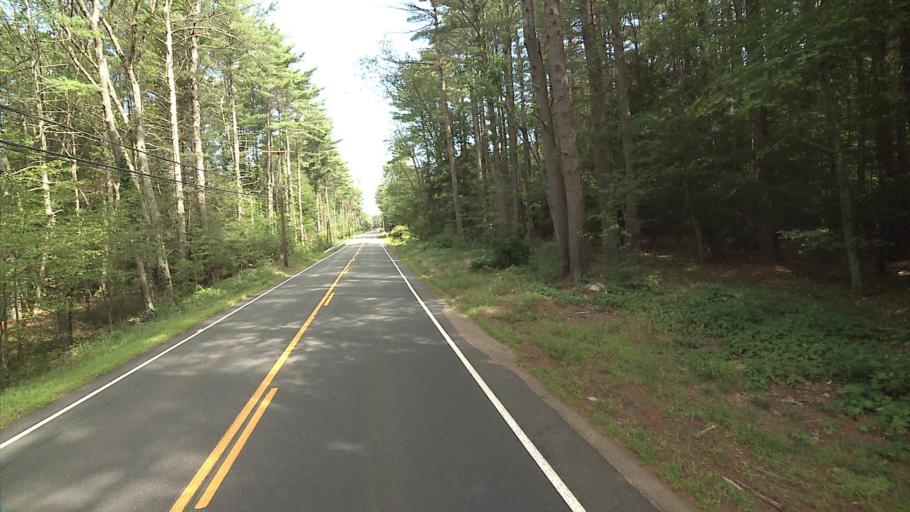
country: US
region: Connecticut
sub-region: Tolland County
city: Stafford
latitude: 42.0064
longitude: -72.3181
